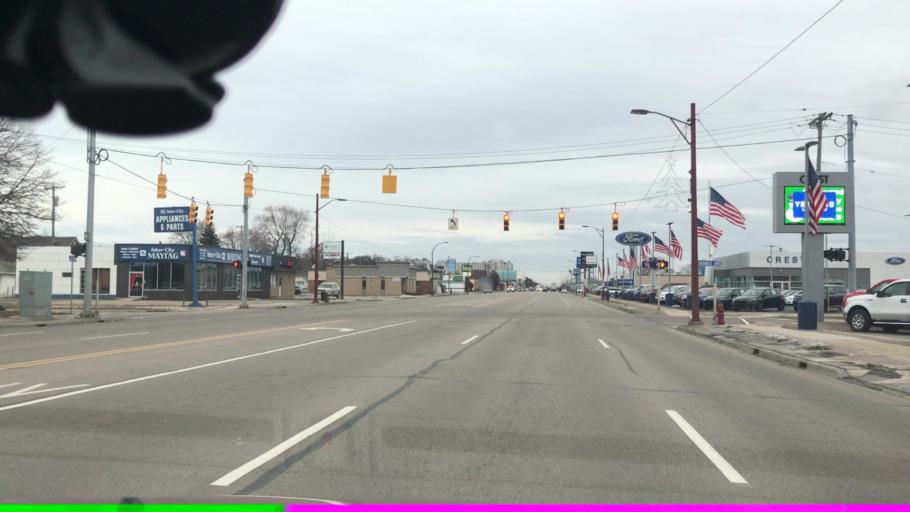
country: US
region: Michigan
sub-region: Macomb County
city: Center Line
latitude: 42.4887
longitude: -83.0277
